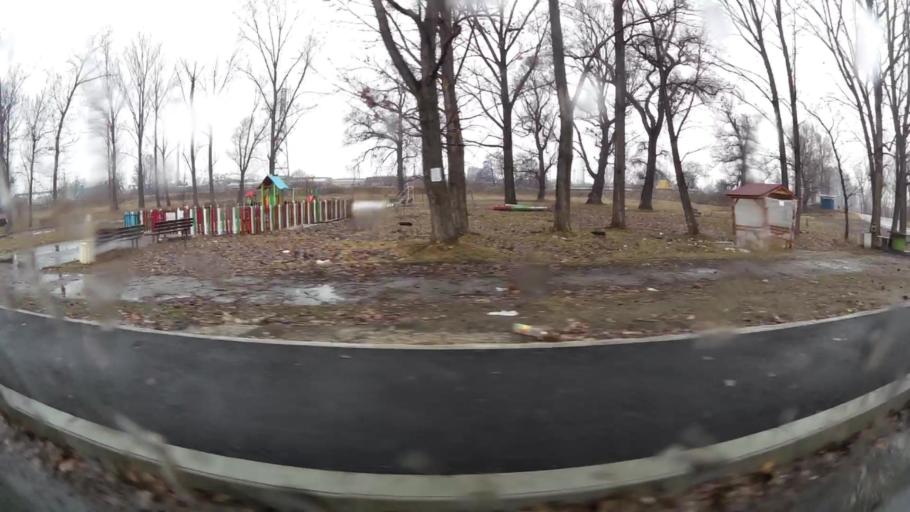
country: BG
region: Sofia-Capital
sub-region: Stolichna Obshtina
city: Sofia
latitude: 42.6645
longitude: 23.4227
